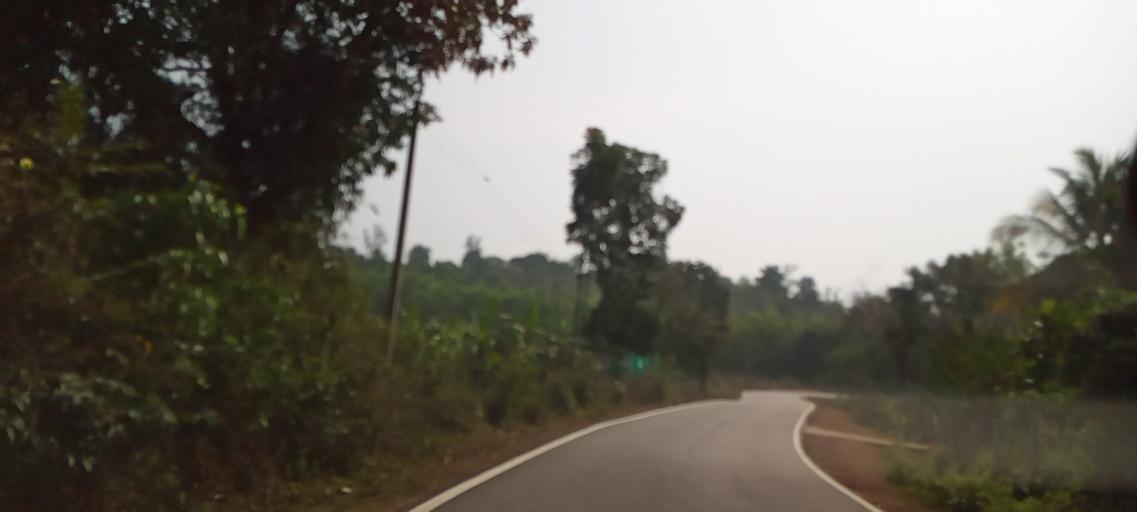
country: IN
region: Karnataka
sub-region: Udupi
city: Hosangadi
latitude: 13.5445
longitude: 74.9010
